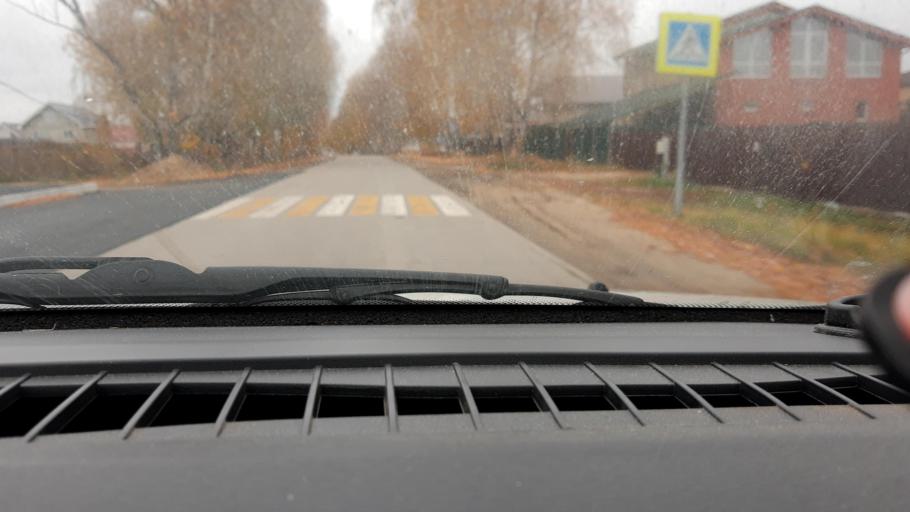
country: RU
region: Nizjnij Novgorod
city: Neklyudovo
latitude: 56.4078
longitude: 44.0163
